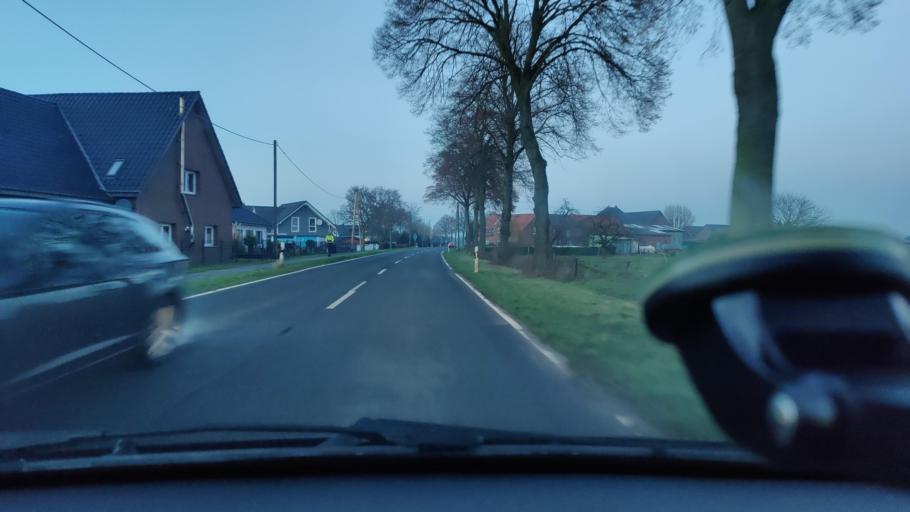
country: DE
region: North Rhine-Westphalia
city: Rheinberg
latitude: 51.5959
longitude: 6.6100
